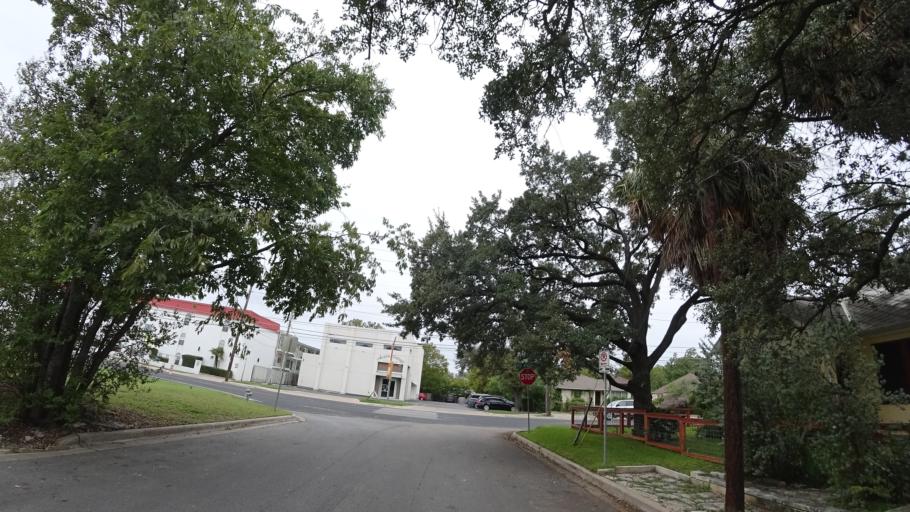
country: US
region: Texas
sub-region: Travis County
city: Austin
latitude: 30.3026
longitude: -97.7207
